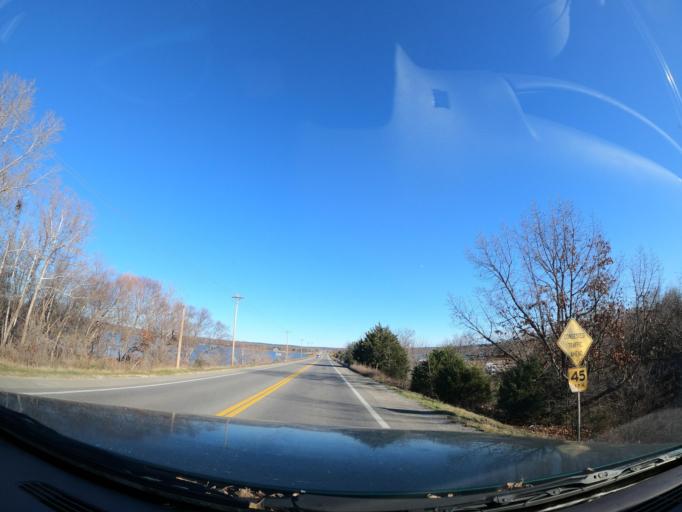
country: US
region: Oklahoma
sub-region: Pittsburg County
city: Longtown
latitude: 35.2392
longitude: -95.5109
